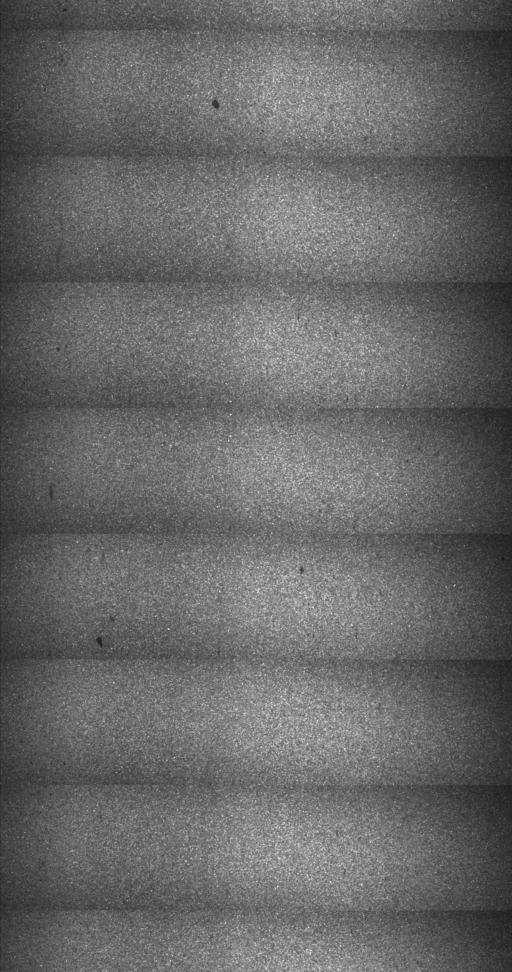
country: US
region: Vermont
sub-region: Bennington County
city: North Bennington
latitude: 42.9093
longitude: -73.2212
